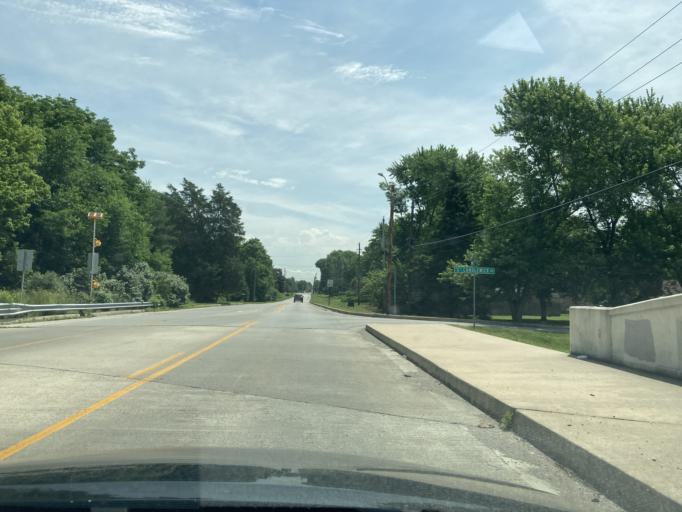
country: US
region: Indiana
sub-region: Marion County
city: Meridian Hills
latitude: 39.8678
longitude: -86.2215
